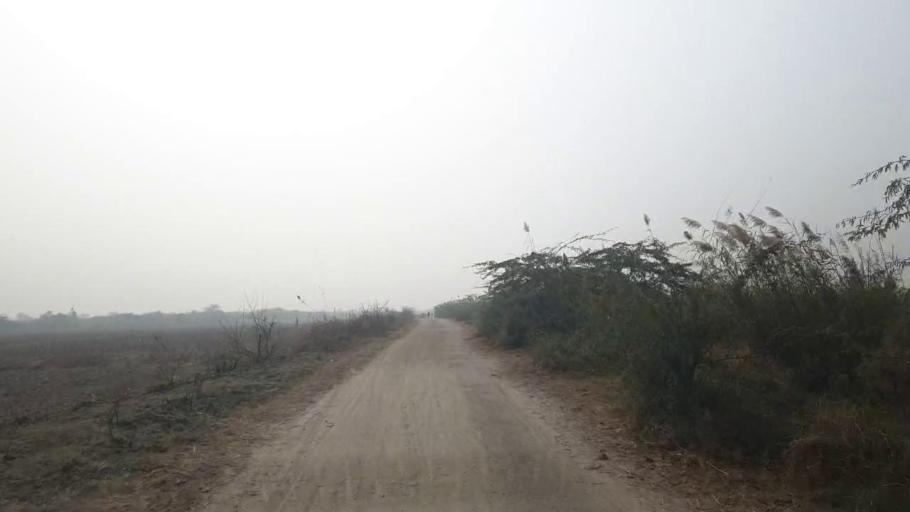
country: PK
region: Sindh
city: Bhit Shah
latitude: 25.7950
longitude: 68.5597
